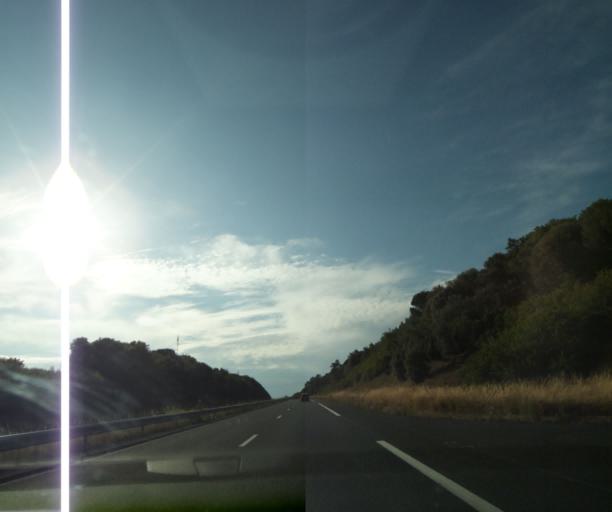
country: FR
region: Poitou-Charentes
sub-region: Departement de la Charente-Maritime
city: Bords
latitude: 45.8983
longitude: -0.7561
